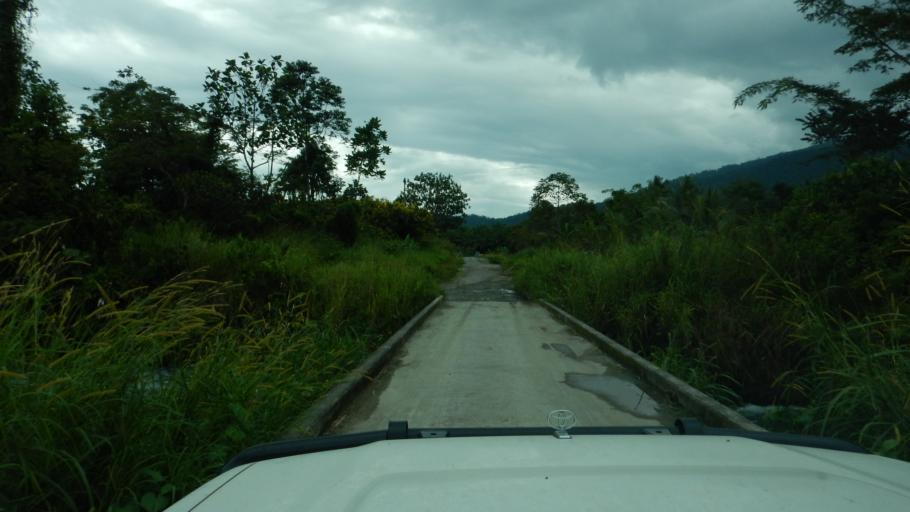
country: PG
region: Northern Province
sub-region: Sohe
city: Kokoda
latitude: -8.9179
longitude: 147.8722
